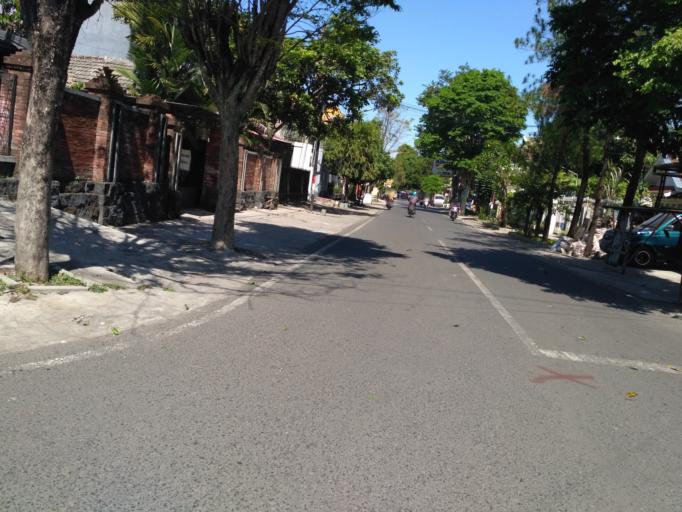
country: ID
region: East Java
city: Malang
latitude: -7.9771
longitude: 112.6645
